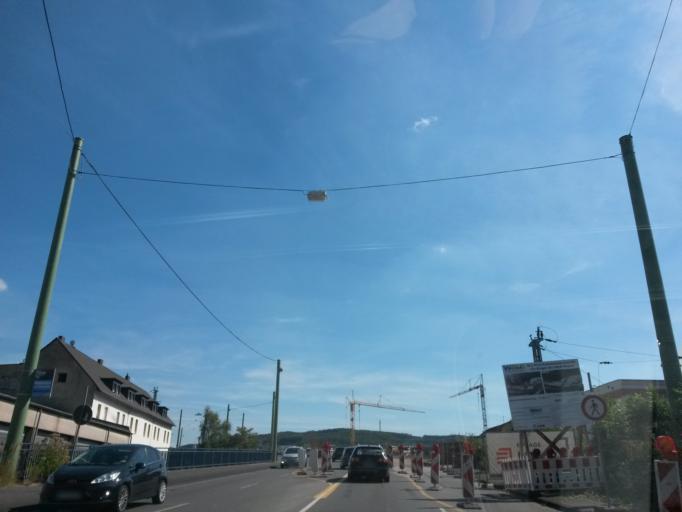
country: DE
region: North Rhine-Westphalia
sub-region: Regierungsbezirk Arnsberg
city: Hagen
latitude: 51.3685
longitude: 7.4590
